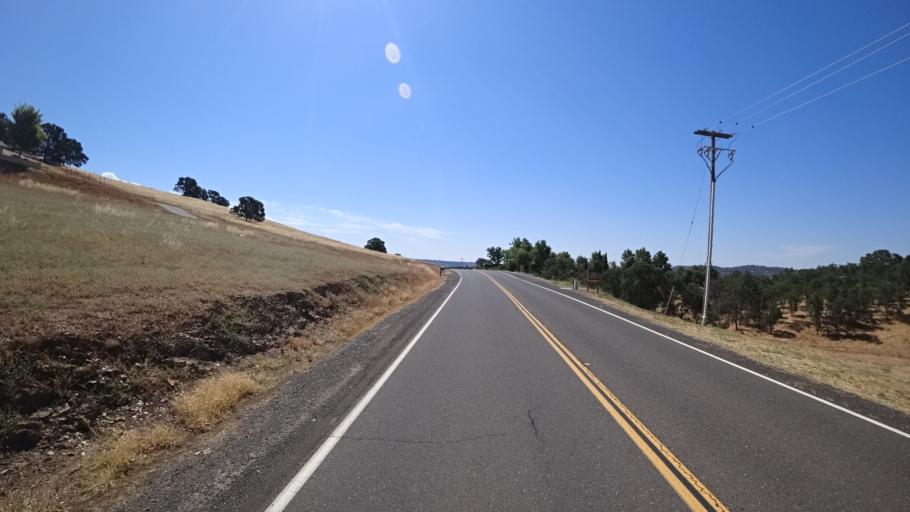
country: US
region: California
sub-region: Calaveras County
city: Copperopolis
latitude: 37.9238
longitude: -120.6349
